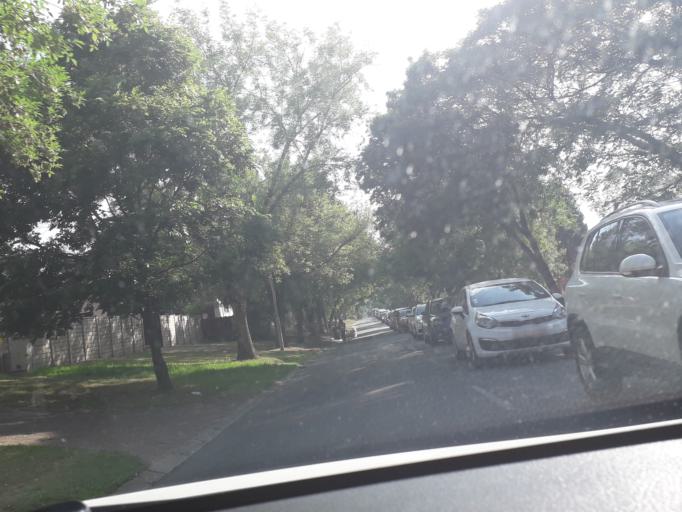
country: ZA
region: Gauteng
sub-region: City of Johannesburg Metropolitan Municipality
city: Diepsloot
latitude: -26.0564
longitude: 27.9797
